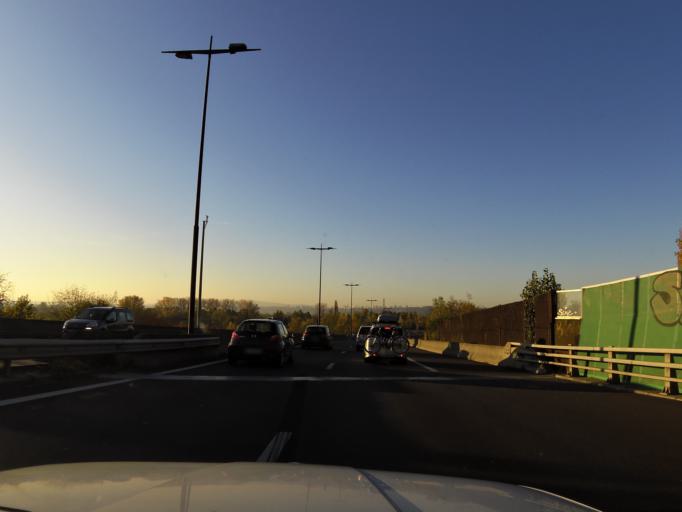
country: FR
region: Rhone-Alpes
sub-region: Departement du Rhone
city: Decines-Charpieu
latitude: 45.7799
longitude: 4.9601
